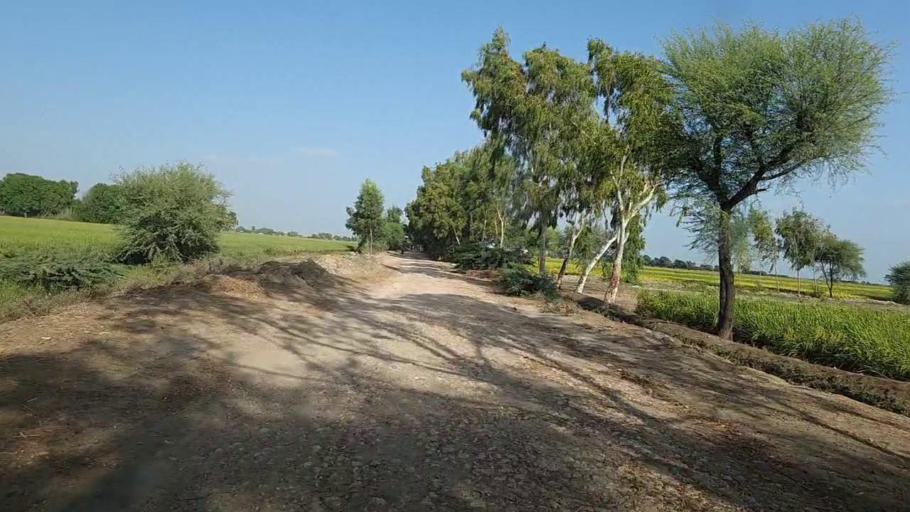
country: PK
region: Sindh
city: Kario
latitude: 24.5996
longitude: 68.5141
